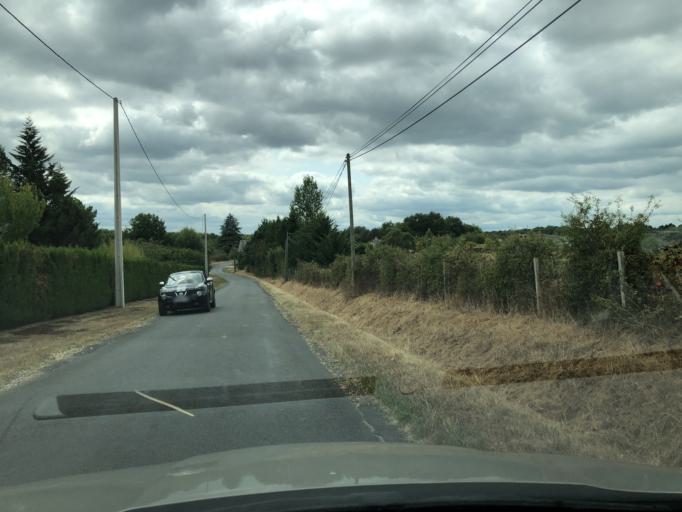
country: FR
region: Centre
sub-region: Departement d'Indre-et-Loire
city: Mazieres-de-Touraine
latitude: 47.3922
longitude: 0.4585
